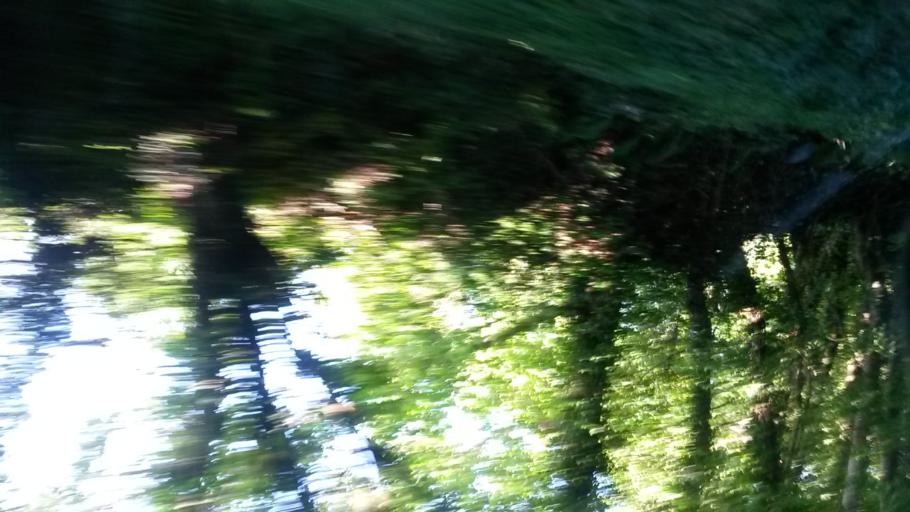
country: IE
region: Leinster
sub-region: An Mhi
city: Ashbourne
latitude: 53.4860
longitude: -6.3318
